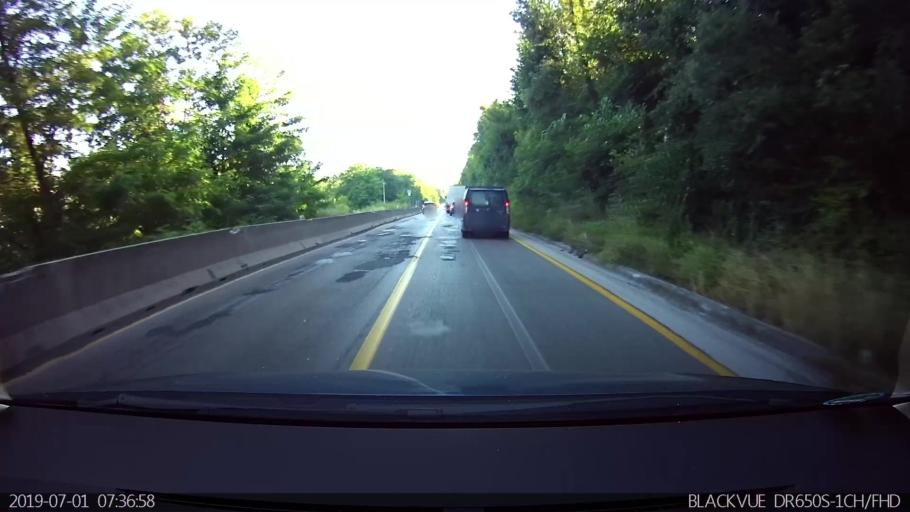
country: IT
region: Latium
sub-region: Provincia di Frosinone
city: Giuliano di Roma
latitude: 41.5346
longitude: 13.2665
